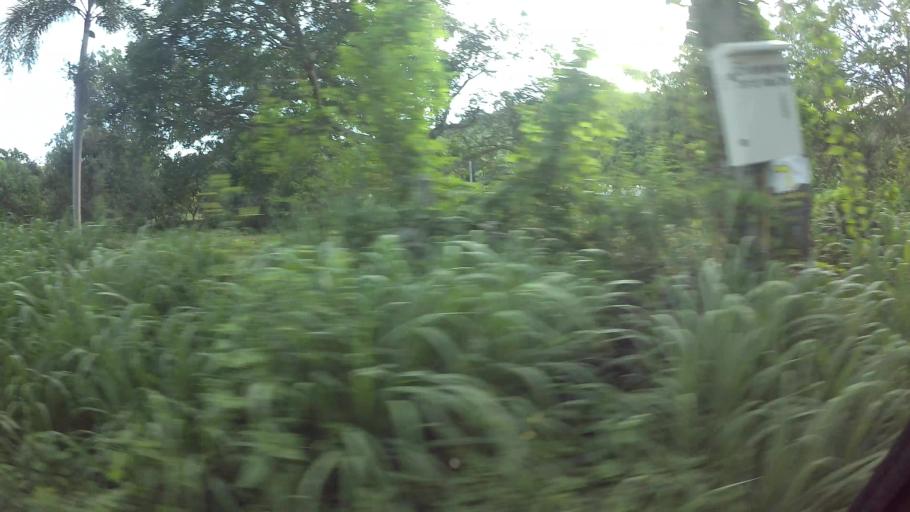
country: TH
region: Chon Buri
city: Sattahip
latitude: 12.6862
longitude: 100.9266
